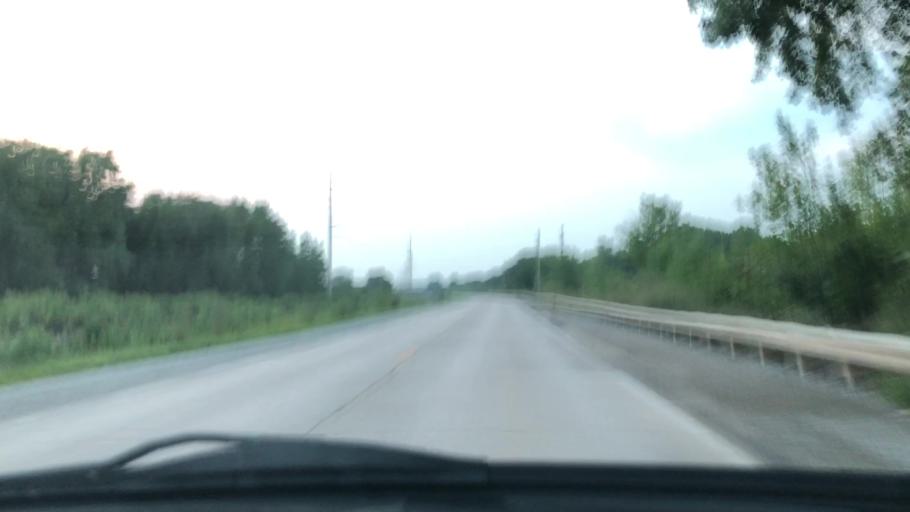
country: US
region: Iowa
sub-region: Johnson County
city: North Liberty
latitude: 41.7933
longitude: -91.6405
